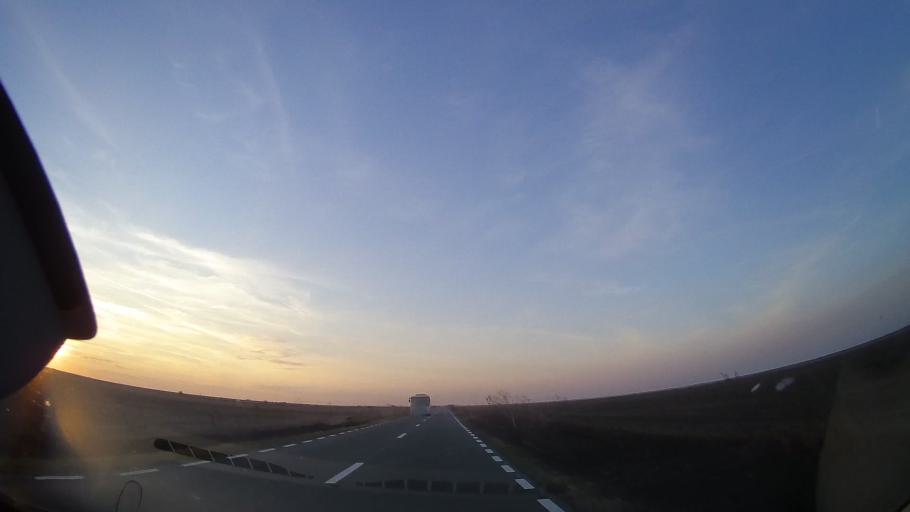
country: RO
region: Constanta
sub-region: Comuna Topraisar
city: Topraisar
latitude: 44.0192
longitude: 28.4227
